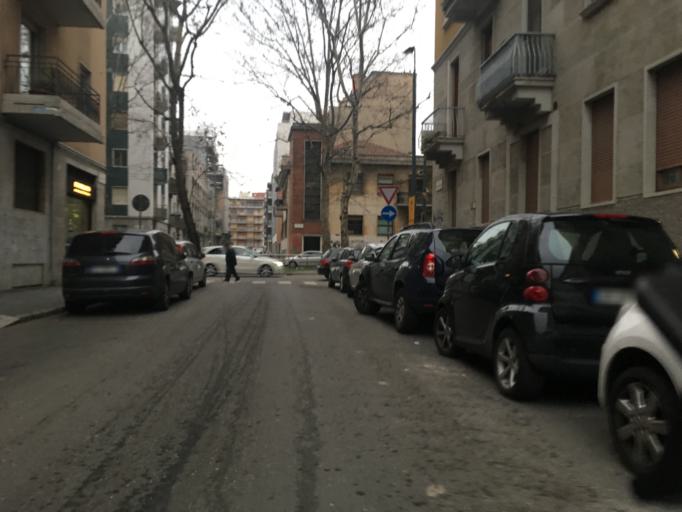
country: IT
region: Lombardy
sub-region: Citta metropolitana di Milano
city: Romano Banco
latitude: 45.4508
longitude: 9.1503
